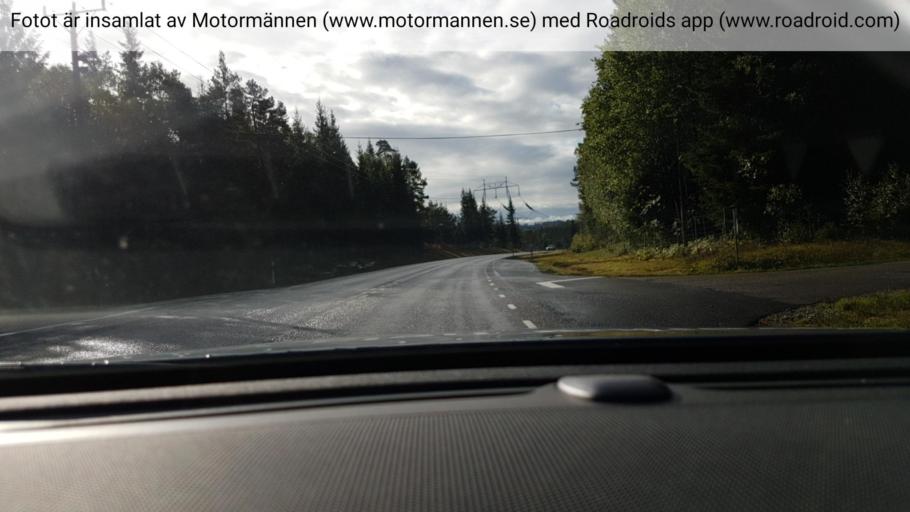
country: SE
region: Vaestra Goetaland
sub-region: Harryda Kommun
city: Hindas
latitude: 57.6468
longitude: 12.4052
